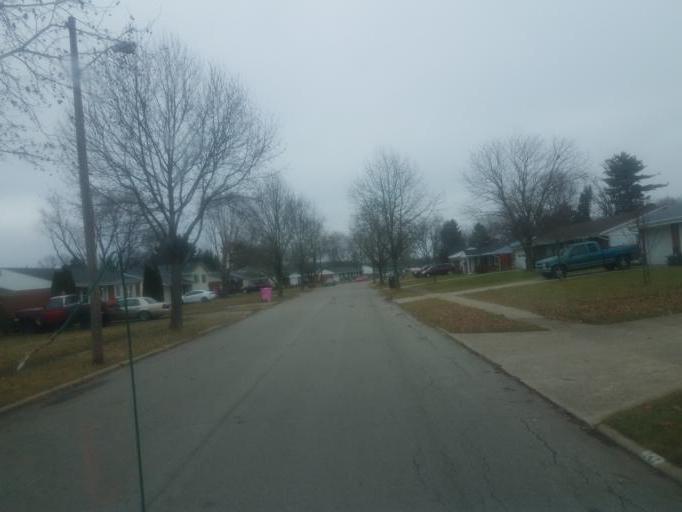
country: US
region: Ohio
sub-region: Richland County
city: Lexington
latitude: 40.6863
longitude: -82.5924
